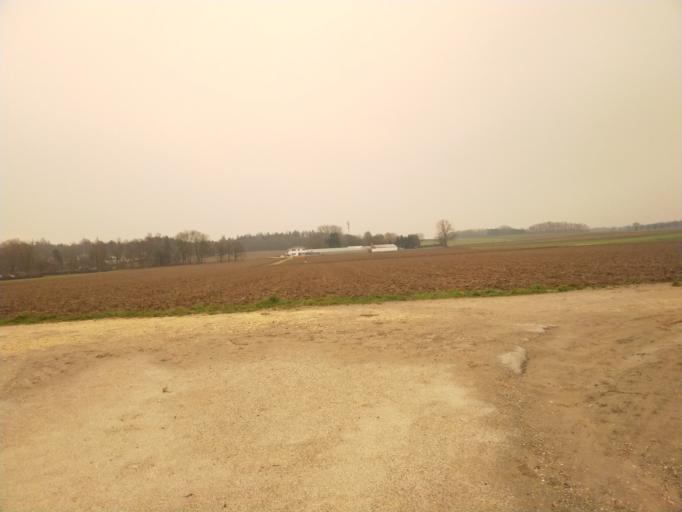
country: DE
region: Bavaria
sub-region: Swabia
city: Guenzburg
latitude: 48.4454
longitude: 10.2919
